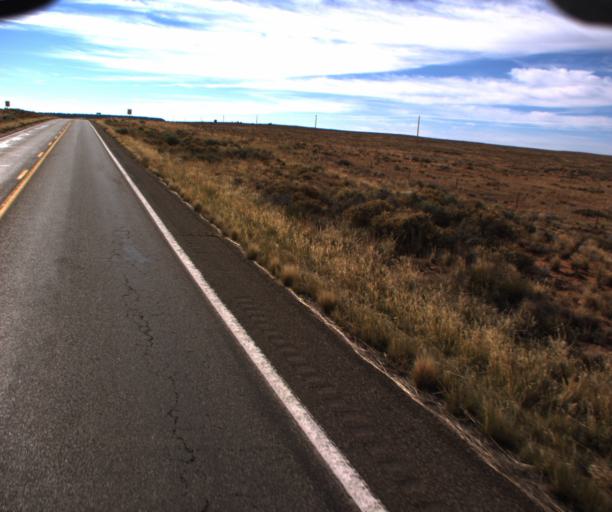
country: US
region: Arizona
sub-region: Coconino County
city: Kaibito
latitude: 36.7080
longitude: -111.2696
